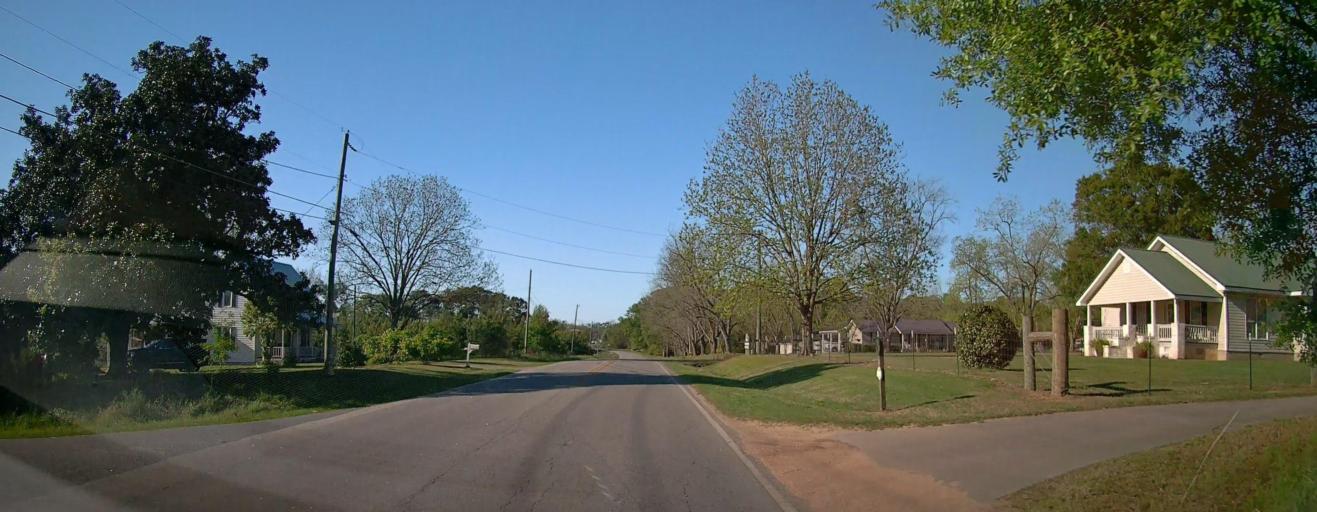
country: US
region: Georgia
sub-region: Ben Hill County
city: Fitzgerald
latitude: 31.7249
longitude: -83.2354
